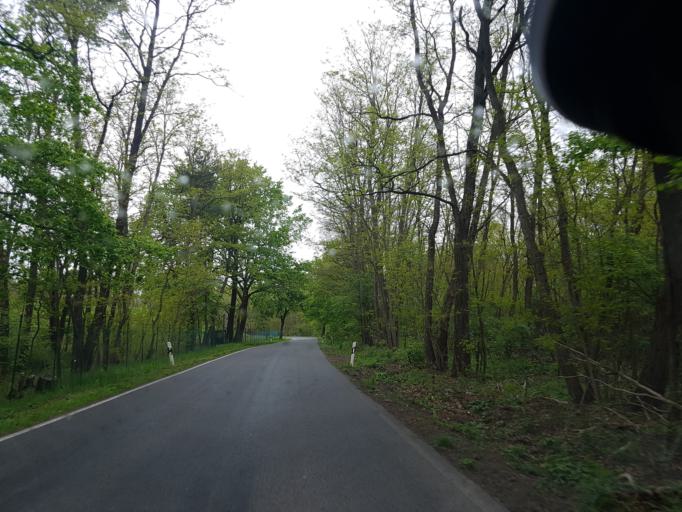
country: DE
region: Brandenburg
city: Drebkau
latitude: 51.6316
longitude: 14.2603
